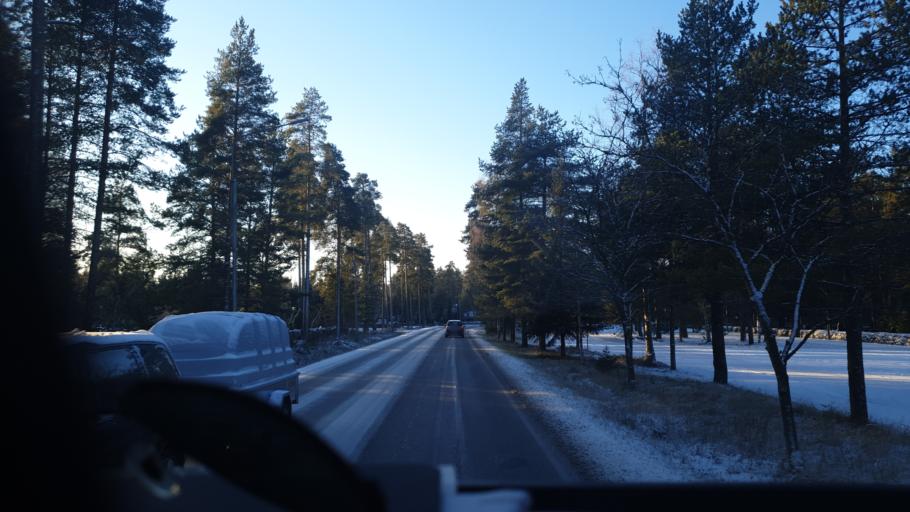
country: FI
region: Central Ostrobothnia
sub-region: Kokkola
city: Kokkola
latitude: 63.8282
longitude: 23.1011
